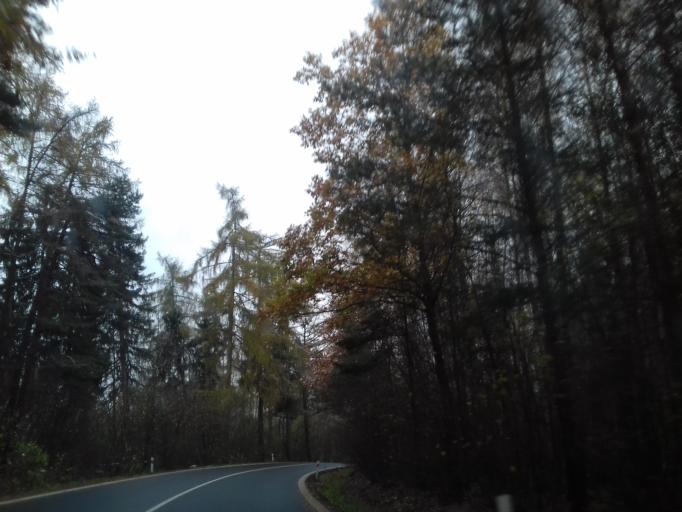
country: CZ
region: Plzensky
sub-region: Okres Domazlice
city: Klenci pod Cerchovem
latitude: 49.4428
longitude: 12.8432
